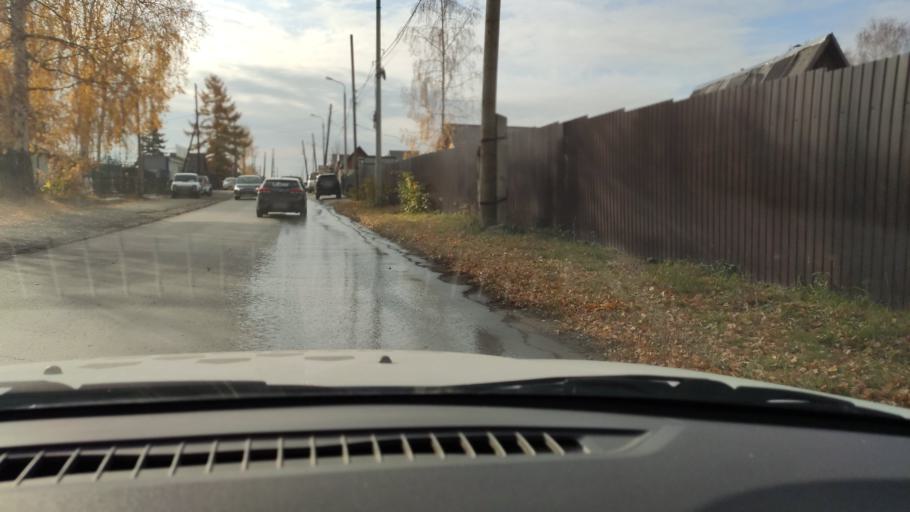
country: RU
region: Perm
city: Kondratovo
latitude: 58.0590
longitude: 56.1236
